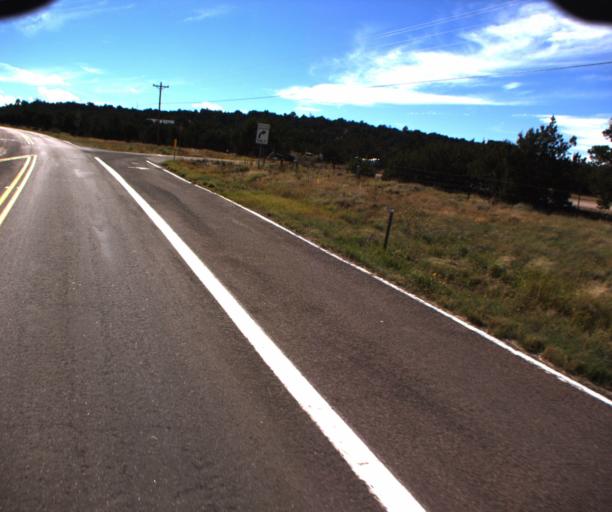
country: US
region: Arizona
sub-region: Navajo County
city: White Mountain Lake
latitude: 34.3172
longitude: -109.7656
